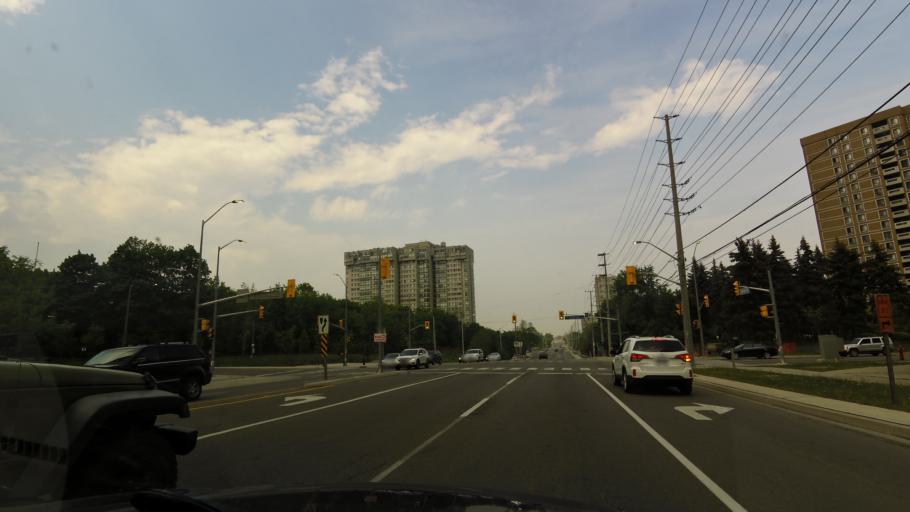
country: CA
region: Ontario
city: Mississauga
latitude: 43.5951
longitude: -79.6332
